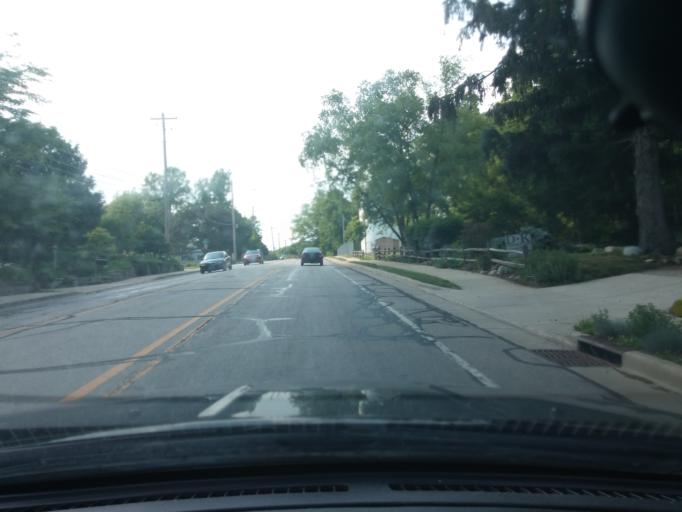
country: US
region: Indiana
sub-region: Tippecanoe County
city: West Lafayette
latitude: 40.4394
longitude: -86.9081
